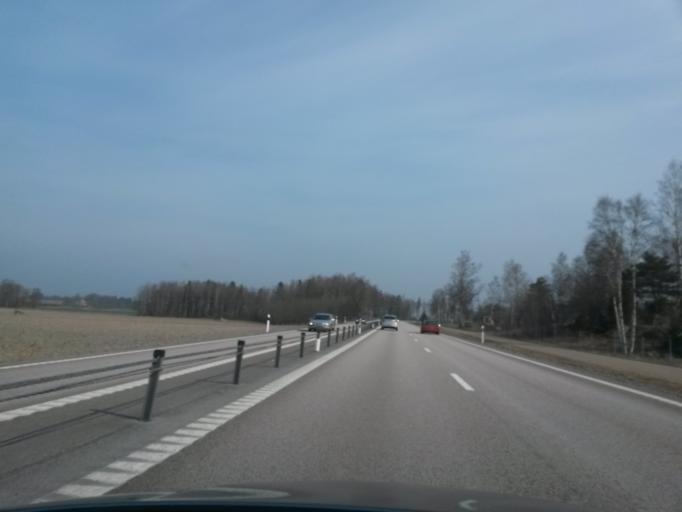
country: SE
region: Vaestra Goetaland
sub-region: Mariestads Kommun
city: Mariestad
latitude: 58.7586
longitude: 13.9688
